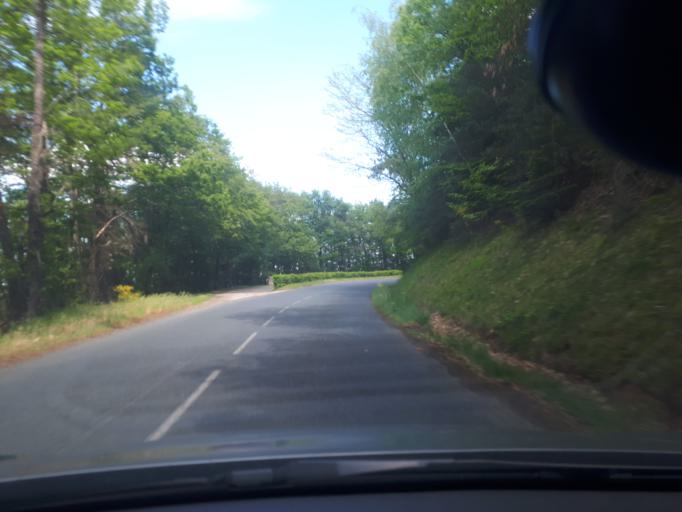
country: FR
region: Rhone-Alpes
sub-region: Departement du Rhone
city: Saint-Martin-en-Haut
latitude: 45.6546
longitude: 4.5834
